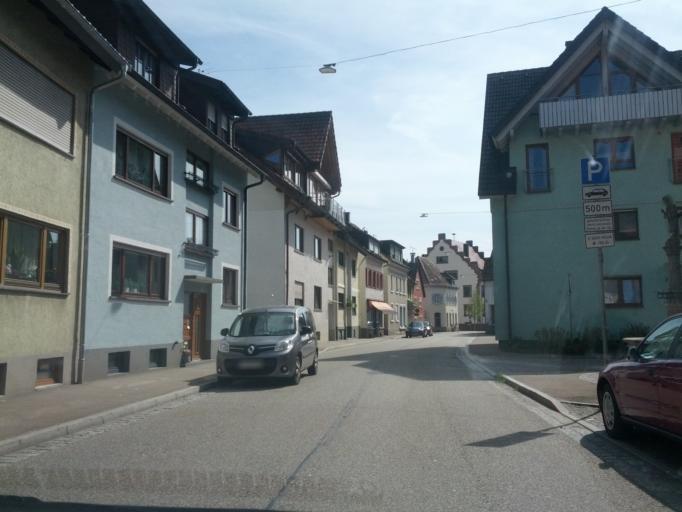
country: DE
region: Baden-Wuerttemberg
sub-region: Freiburg Region
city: Elzach
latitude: 48.1765
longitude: 8.0727
